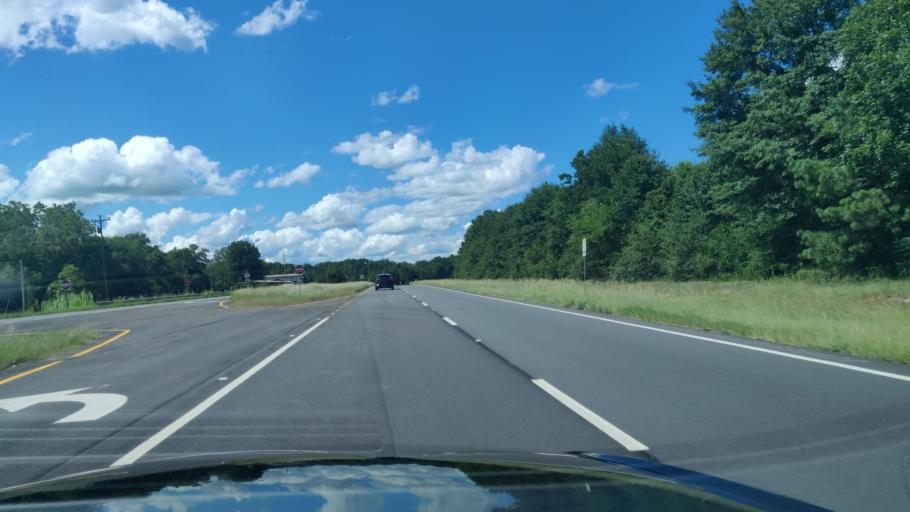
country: US
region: Georgia
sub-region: Stewart County
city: Richland
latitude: 32.1699
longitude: -84.7071
